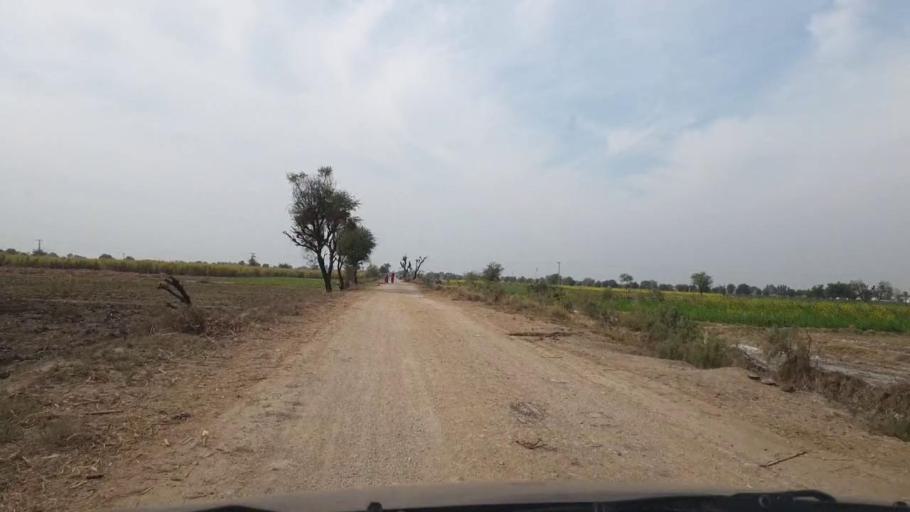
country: PK
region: Sindh
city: Sinjhoro
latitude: 26.0830
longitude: 68.8318
